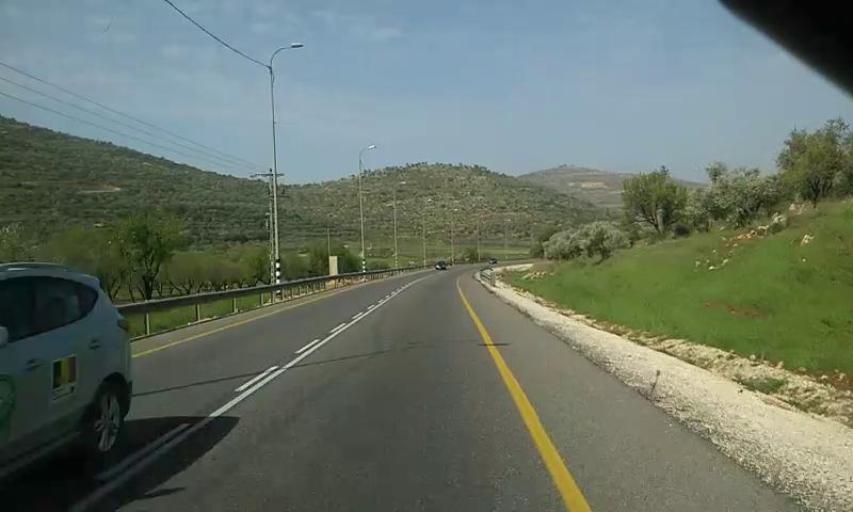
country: PS
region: West Bank
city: Al Lubban ash Sharqiyah
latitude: 32.0655
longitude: 35.2475
